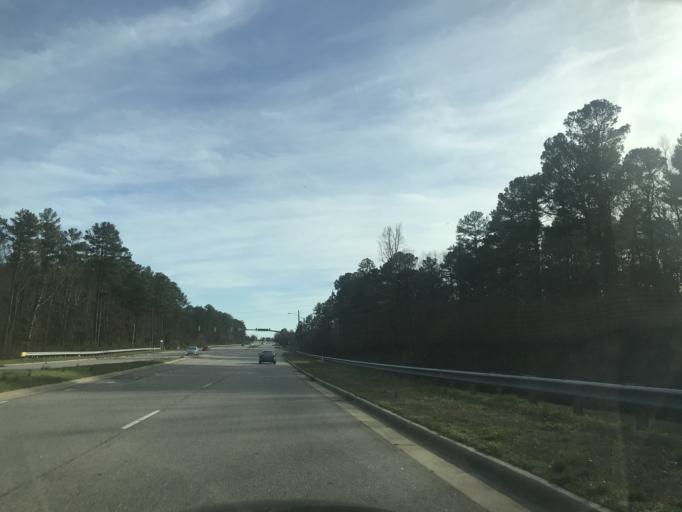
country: US
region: North Carolina
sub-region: Wake County
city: Morrisville
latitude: 35.8870
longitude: -78.8635
